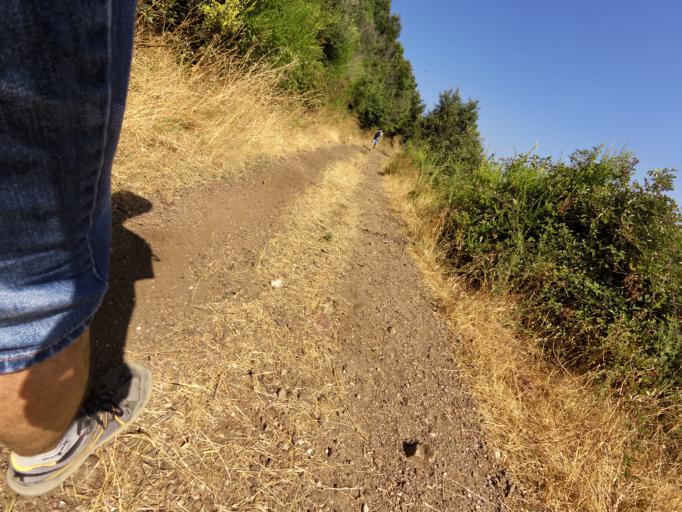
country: IT
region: Calabria
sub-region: Provincia di Reggio Calabria
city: Bivongi
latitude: 38.5013
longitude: 16.4483
